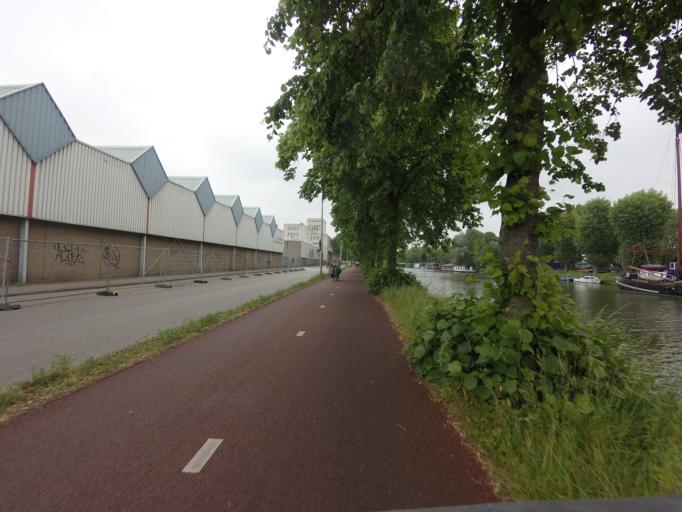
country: NL
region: Utrecht
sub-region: Gemeente Utrecht
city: Lunetten
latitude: 52.0643
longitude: 5.1124
